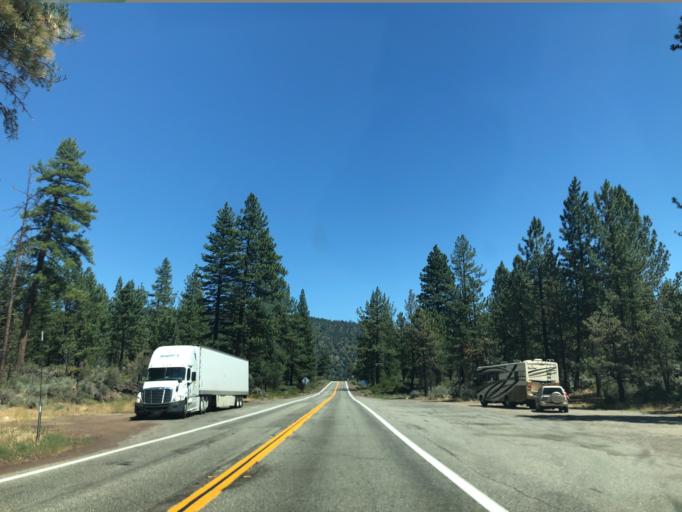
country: US
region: California
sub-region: Shasta County
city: Burney
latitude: 40.6804
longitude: -121.4234
